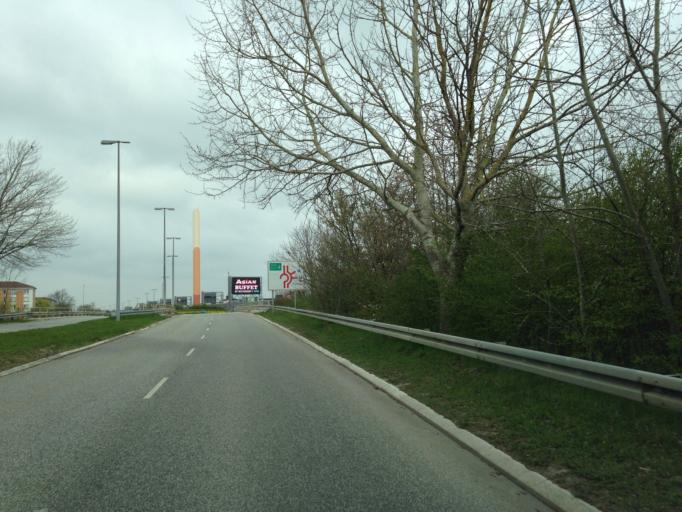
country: DK
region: Capital Region
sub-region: Ishoj Kommune
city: Ishoj
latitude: 55.5959
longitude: 12.3331
